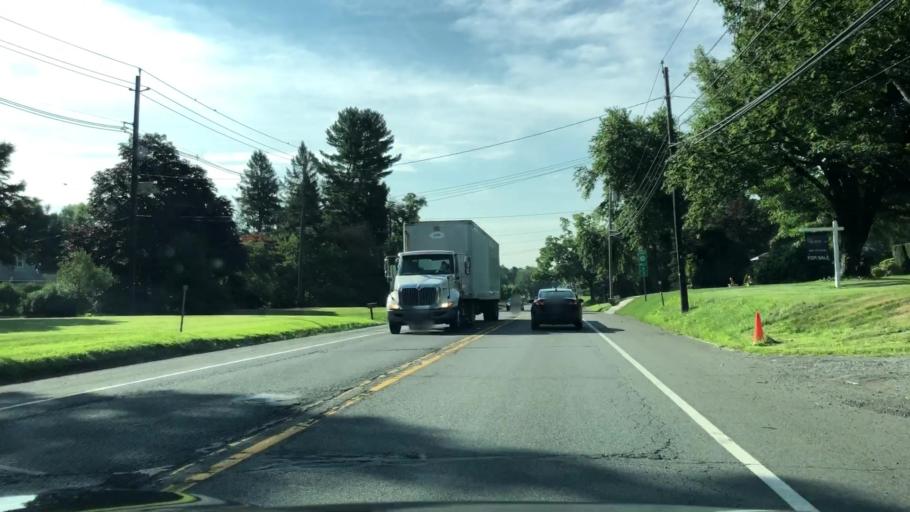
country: US
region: New Jersey
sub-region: Mercer County
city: Pennington
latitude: 40.3127
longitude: -74.7911
